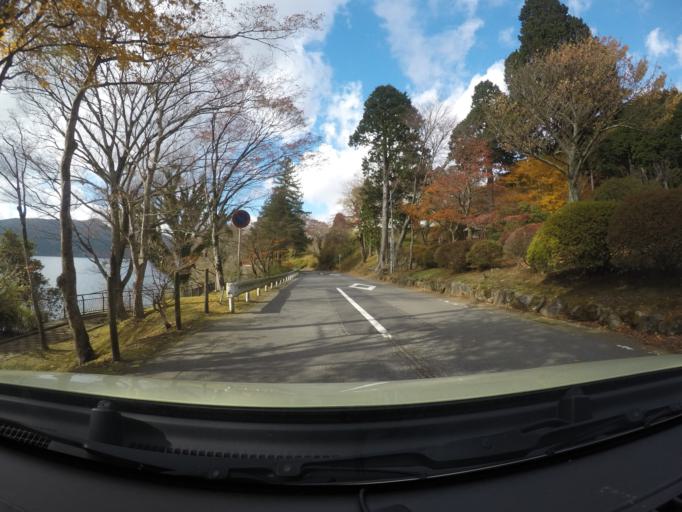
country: JP
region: Kanagawa
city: Hakone
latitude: 35.2039
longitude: 139.0224
